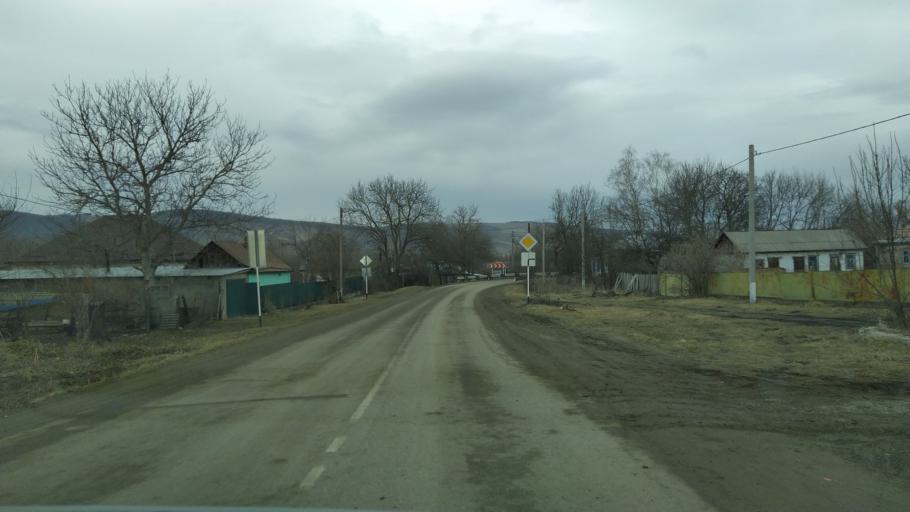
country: RU
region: Krasnodarskiy
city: Peredovaya
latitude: 44.1185
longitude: 41.4727
